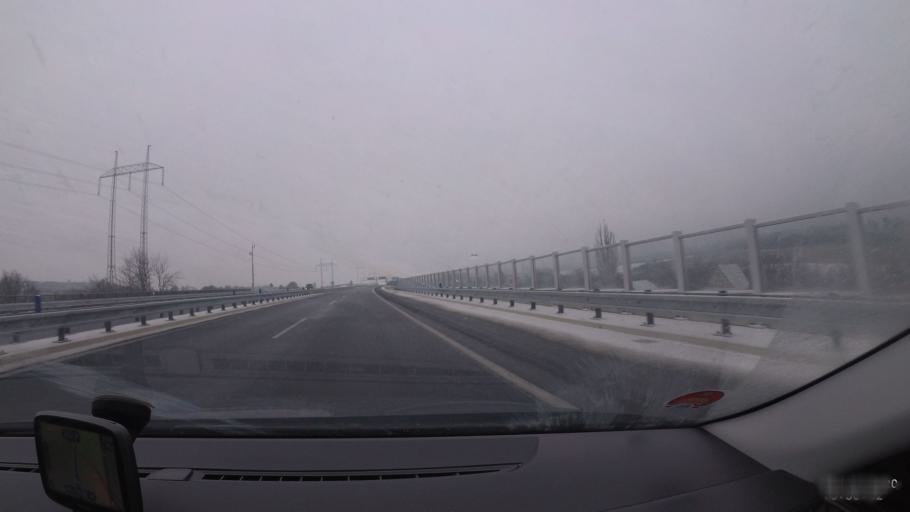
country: CZ
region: Central Bohemia
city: Revnicov
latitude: 50.1774
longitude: 13.7779
